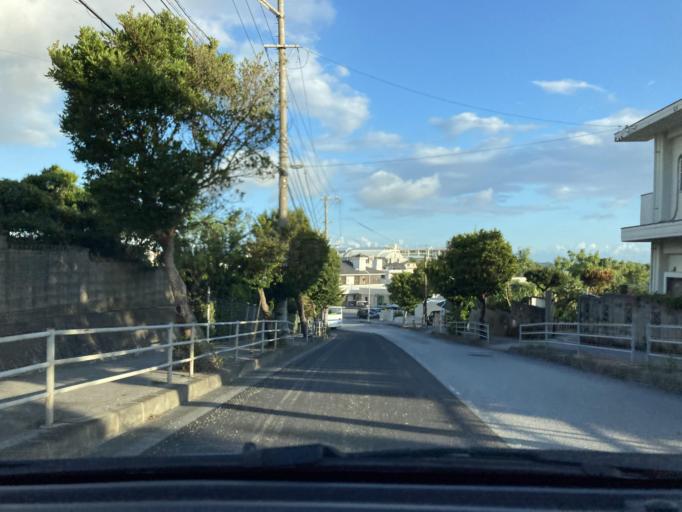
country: JP
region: Okinawa
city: Naha-shi
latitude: 26.2040
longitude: 127.7192
